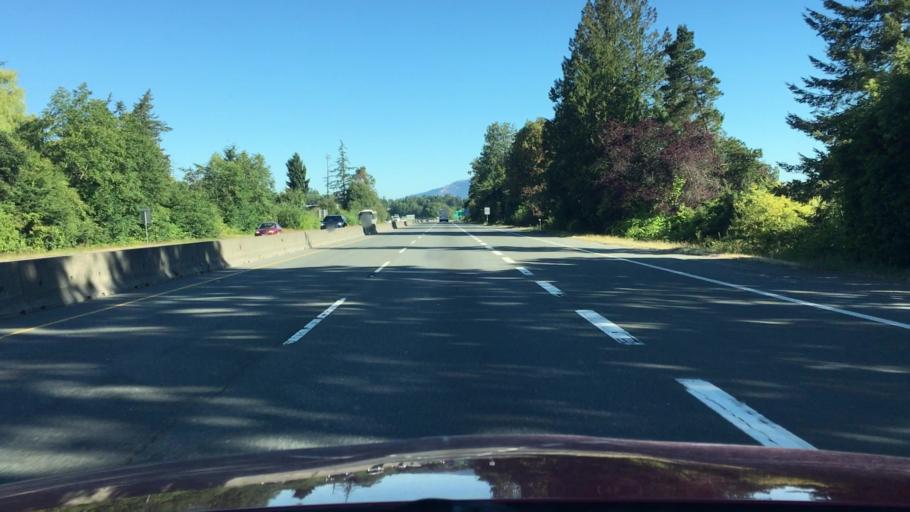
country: CA
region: British Columbia
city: North Saanich
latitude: 48.6162
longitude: -123.4042
